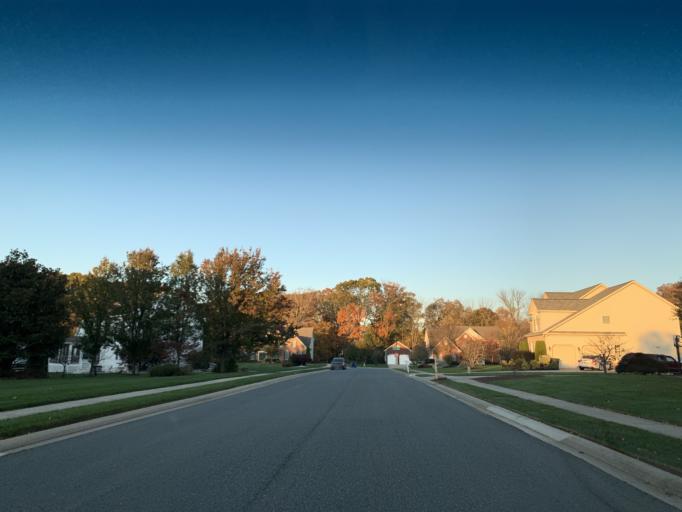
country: US
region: Maryland
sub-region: Harford County
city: South Bel Air
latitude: 39.5564
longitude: -76.3081
